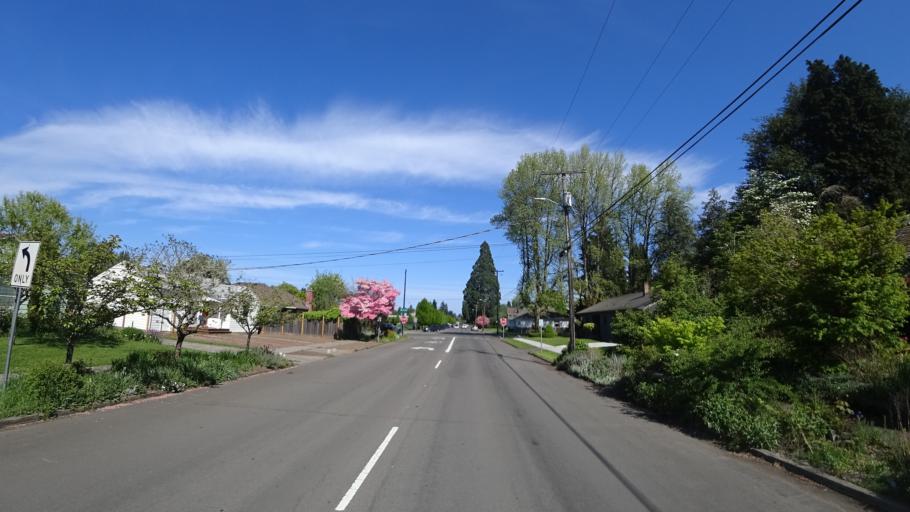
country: US
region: Oregon
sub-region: Washington County
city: Hillsboro
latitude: 45.5238
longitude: -122.9815
